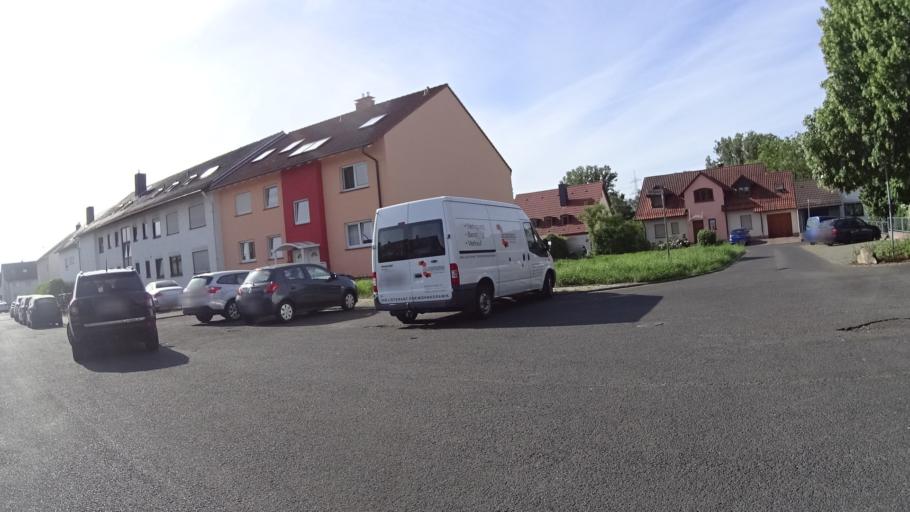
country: DE
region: Bavaria
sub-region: Regierungsbezirk Unterfranken
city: Mainaschaff
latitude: 49.9769
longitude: 9.0884
